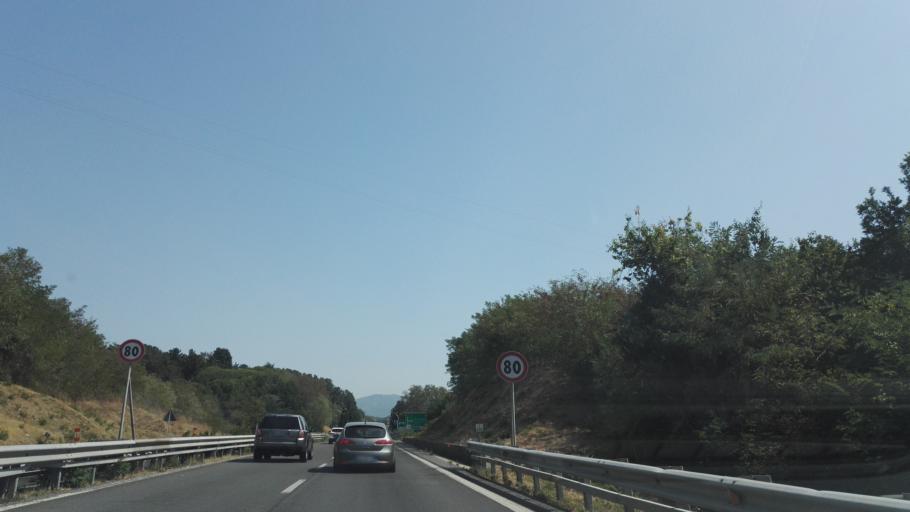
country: IT
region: Calabria
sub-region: Provincia di Cosenza
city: Rogliano
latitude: 39.1846
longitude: 16.3045
